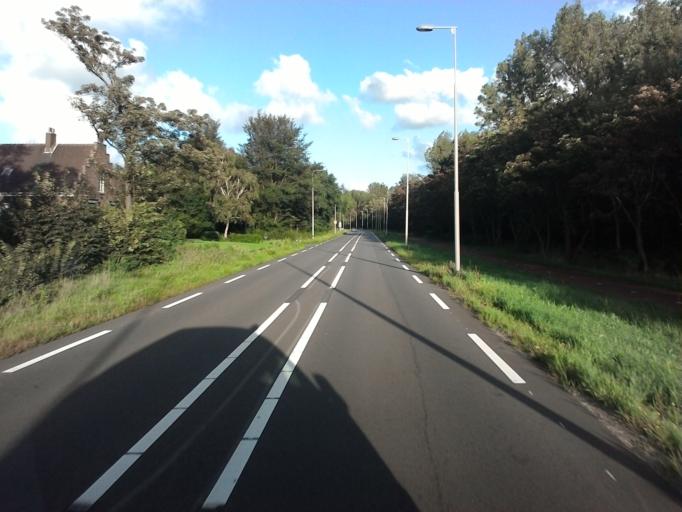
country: NL
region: North Holland
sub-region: Gemeente Beverwijk
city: Beverwijk
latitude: 52.4887
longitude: 4.6188
